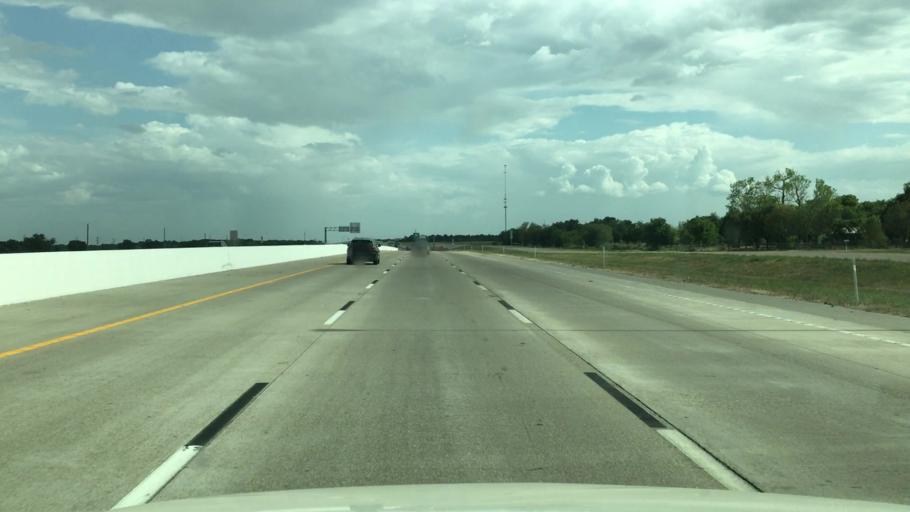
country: US
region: Texas
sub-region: McLennan County
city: West
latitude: 31.7619
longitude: -97.1042
